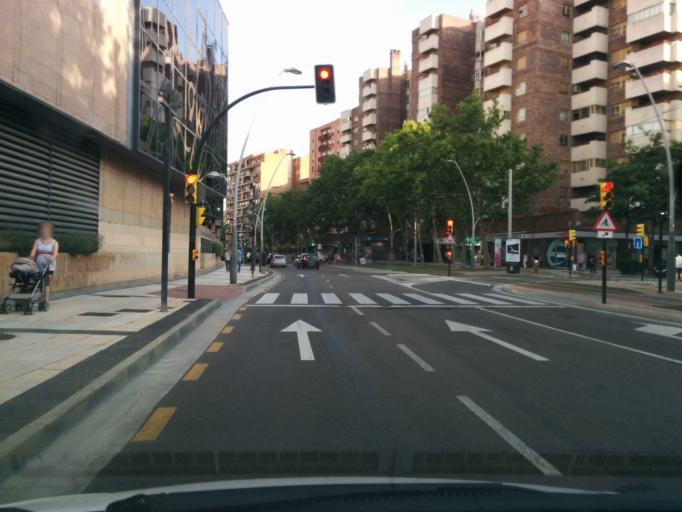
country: ES
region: Aragon
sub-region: Provincia de Zaragoza
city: Almozara
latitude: 41.6709
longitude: -0.8907
